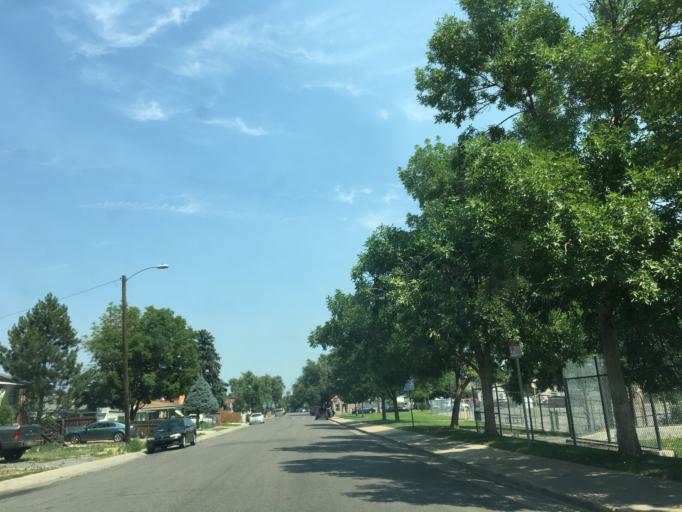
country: US
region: Colorado
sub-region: Jefferson County
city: Lakewood
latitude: 39.7010
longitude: -105.0368
